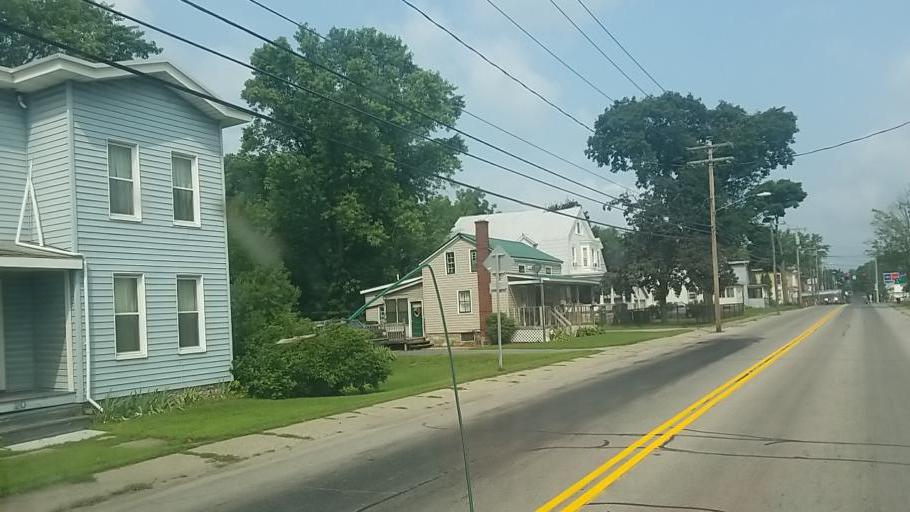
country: US
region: New York
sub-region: Montgomery County
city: Fort Plain
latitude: 42.9332
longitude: -74.6128
